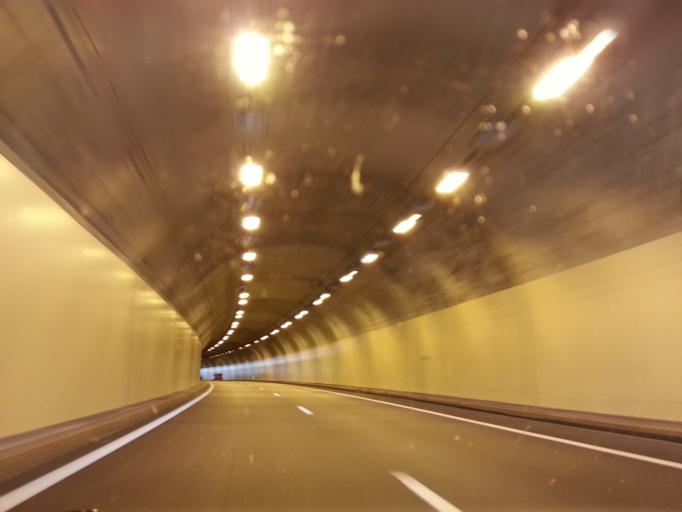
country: FR
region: Rhone-Alpes
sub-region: Departement de la Haute-Savoie
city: Allonzier-la-Caille
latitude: 46.0173
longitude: 6.1028
